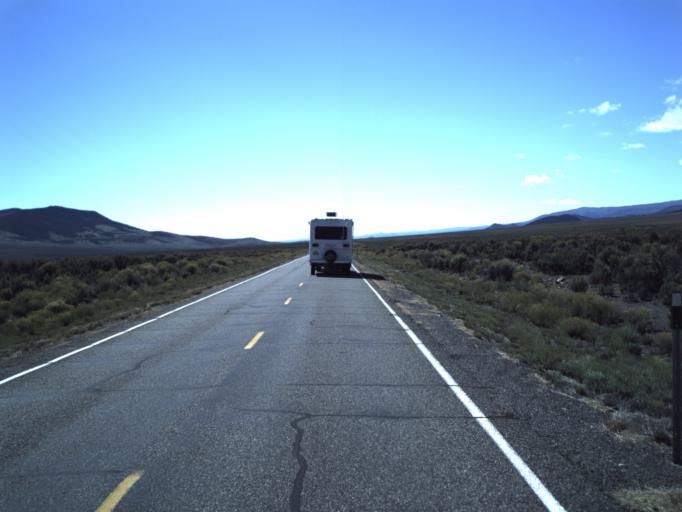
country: US
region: Utah
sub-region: Wayne County
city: Loa
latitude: 38.4058
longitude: -111.9279
